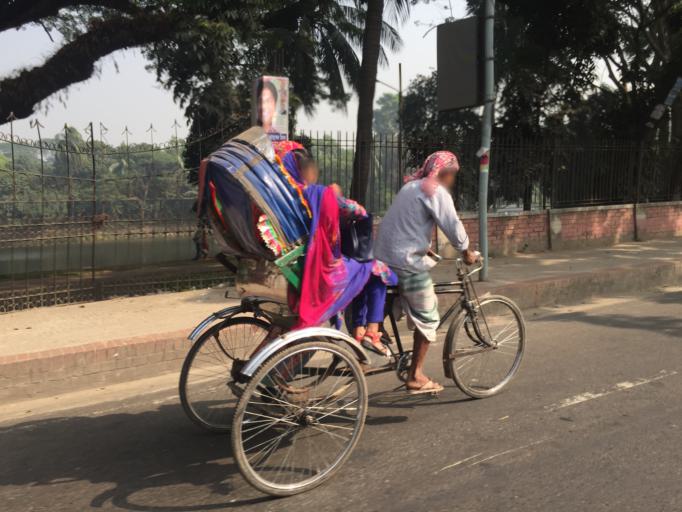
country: BD
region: Dhaka
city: Paltan
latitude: 23.7367
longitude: 90.3998
